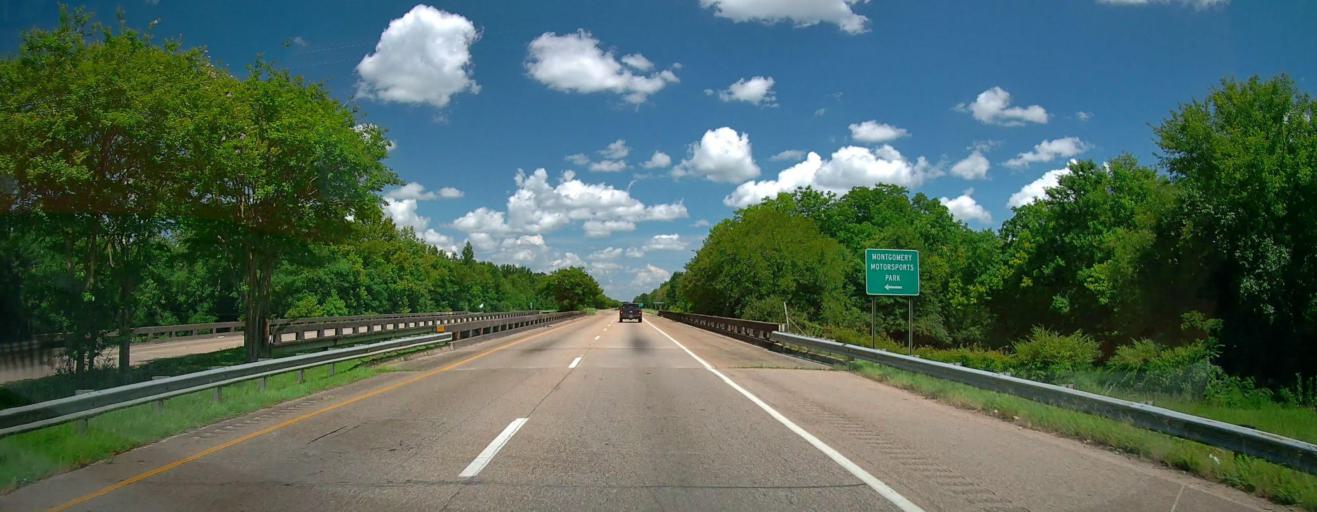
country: US
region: Alabama
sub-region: Montgomery County
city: Montgomery
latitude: 32.4223
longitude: -86.2566
